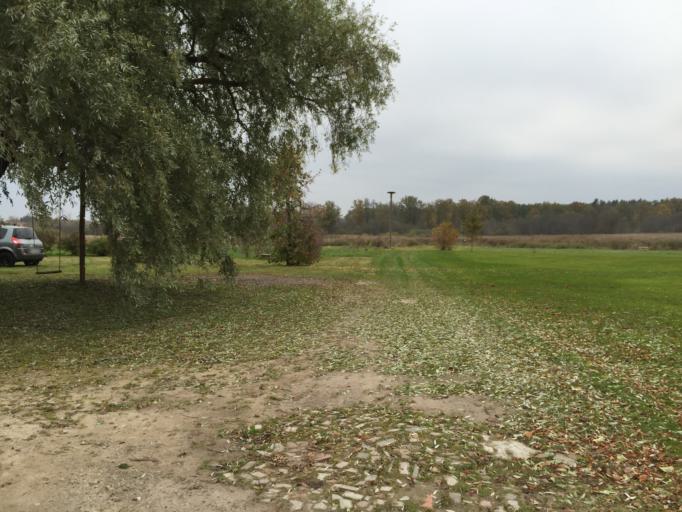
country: LV
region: Ozolnieku
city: Ozolnieki
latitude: 56.6388
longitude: 23.7781
